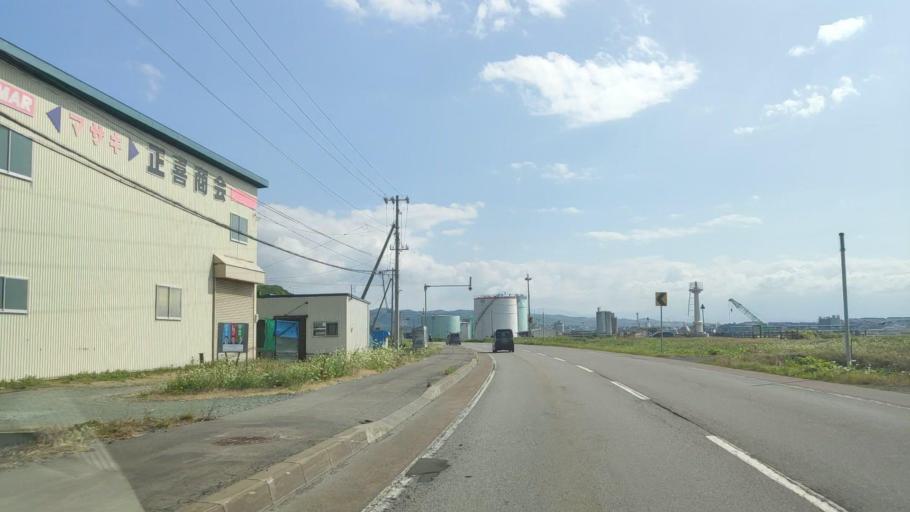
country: JP
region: Hokkaido
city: Rumoi
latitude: 43.9615
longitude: 141.6428
